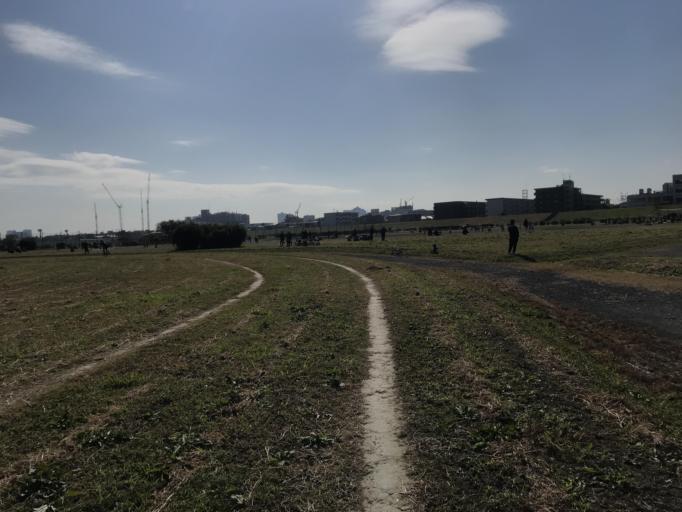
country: JP
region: Kanagawa
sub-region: Kawasaki-shi
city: Kawasaki
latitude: 35.5578
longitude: 139.6874
